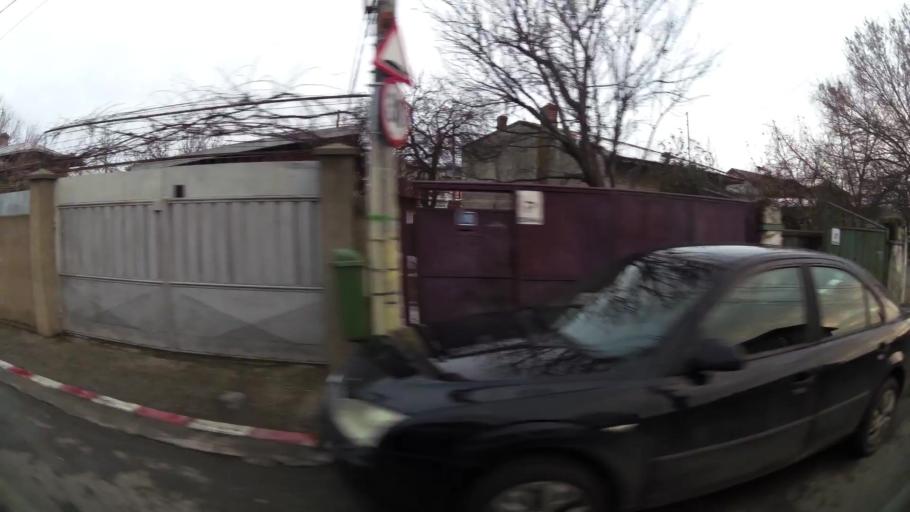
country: RO
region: Ilfov
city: Dobroesti
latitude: 44.4515
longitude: 26.1807
